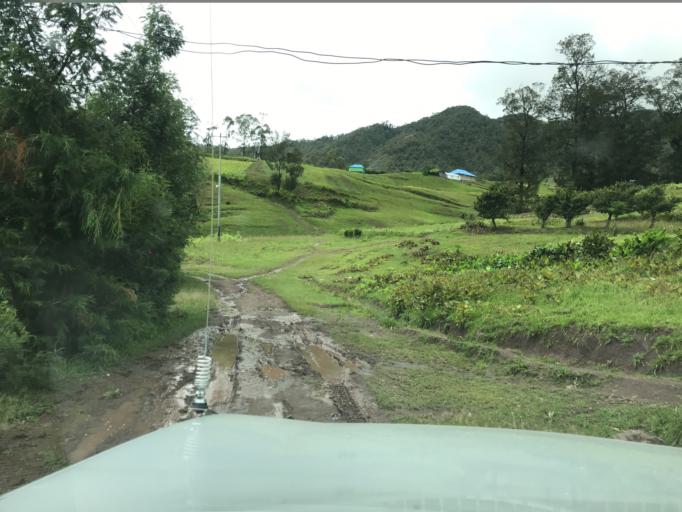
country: TL
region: Ainaro
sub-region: Ainaro
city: Ainaro
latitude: -8.8655
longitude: 125.5544
